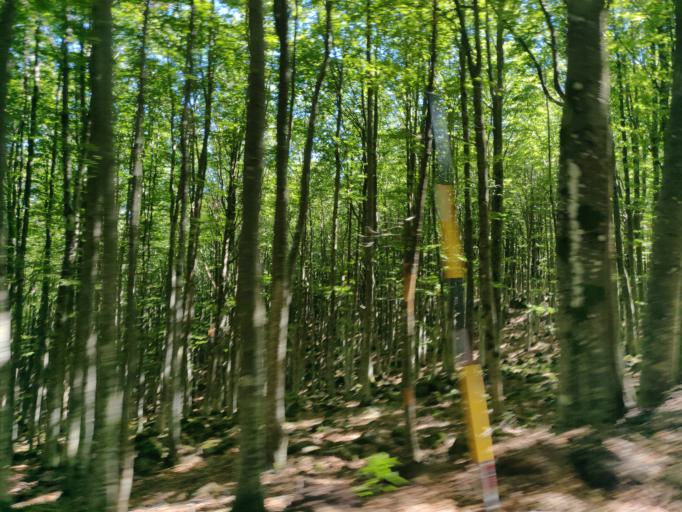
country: IT
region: Tuscany
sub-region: Provincia di Siena
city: Abbadia San Salvatore
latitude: 42.8835
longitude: 11.6234
